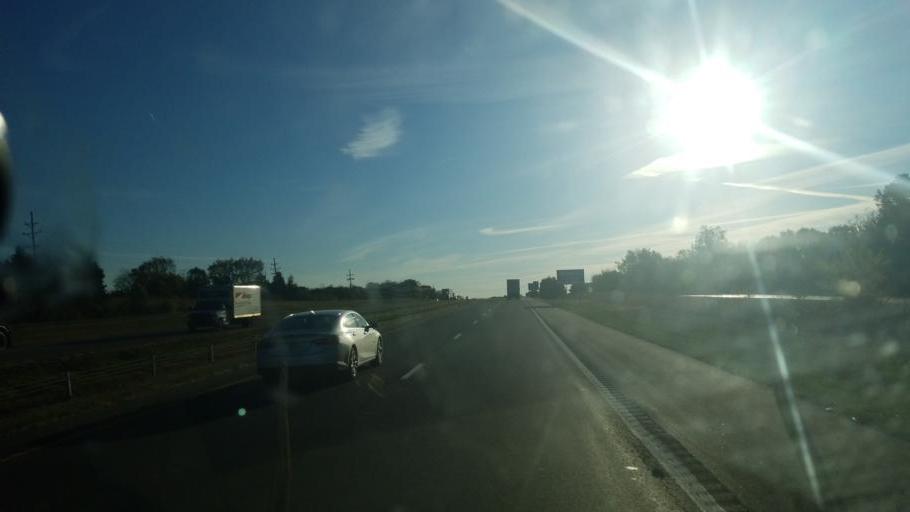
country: US
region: Missouri
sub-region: Saint Charles County
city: Wentzville
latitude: 38.8061
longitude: -90.9115
